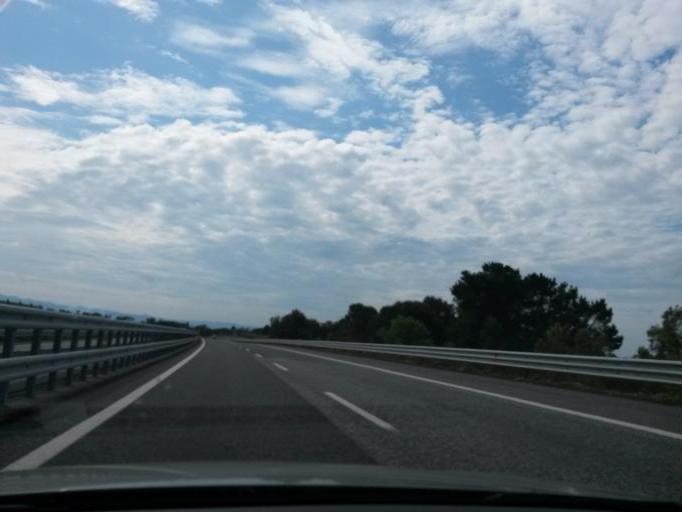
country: IT
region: Tuscany
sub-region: Provincia di Livorno
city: S.P. in Palazzi
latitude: 43.3488
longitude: 10.5157
